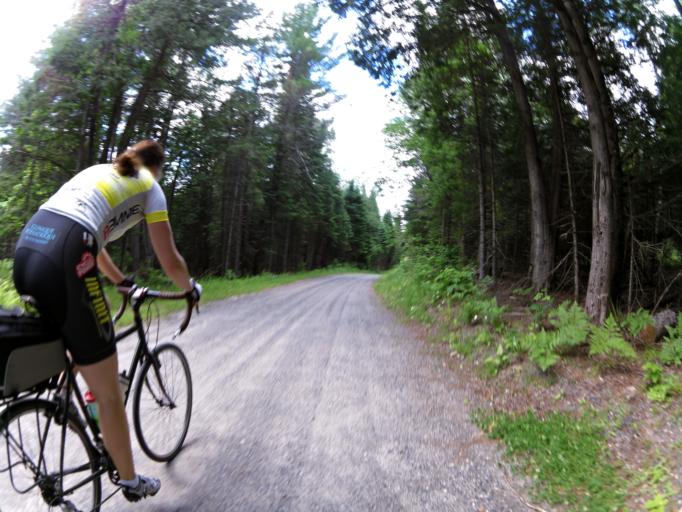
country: CA
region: Ontario
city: Perth
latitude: 45.0710
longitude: -76.4729
